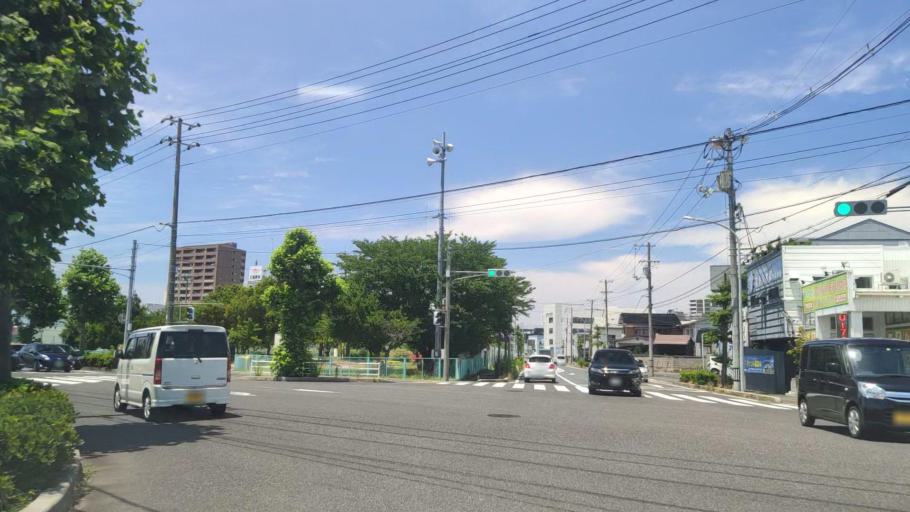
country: JP
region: Tottori
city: Tottori
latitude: 35.4884
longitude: 134.2323
